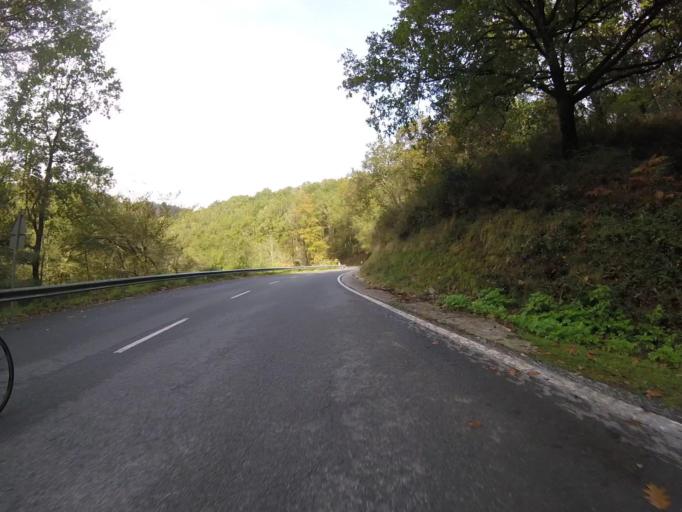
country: ES
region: Navarre
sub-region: Provincia de Navarra
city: Goizueta
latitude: 43.2008
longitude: -1.8571
